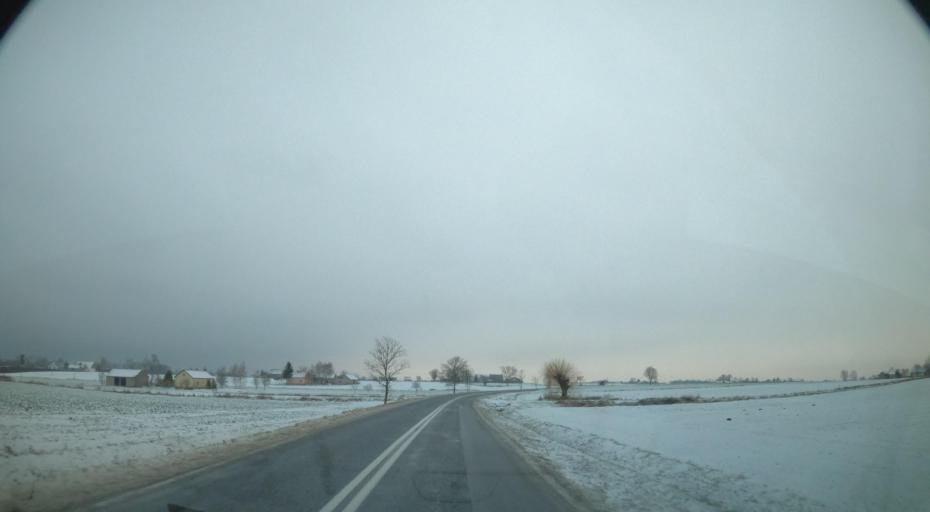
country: PL
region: Kujawsko-Pomorskie
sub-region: Powiat lipnowski
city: Dobrzyn nad Wisla
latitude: 52.6365
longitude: 19.4039
